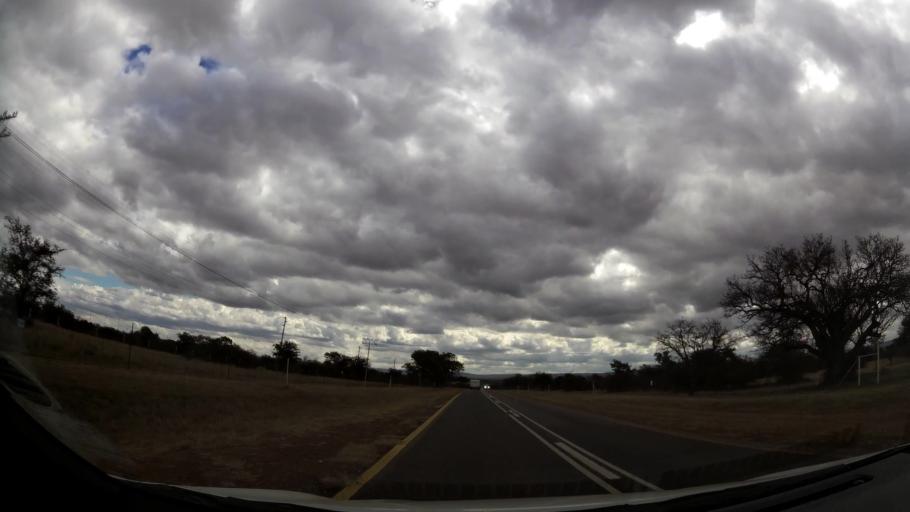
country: ZA
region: Limpopo
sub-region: Waterberg District Municipality
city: Modimolle
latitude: -24.7643
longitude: 28.4606
